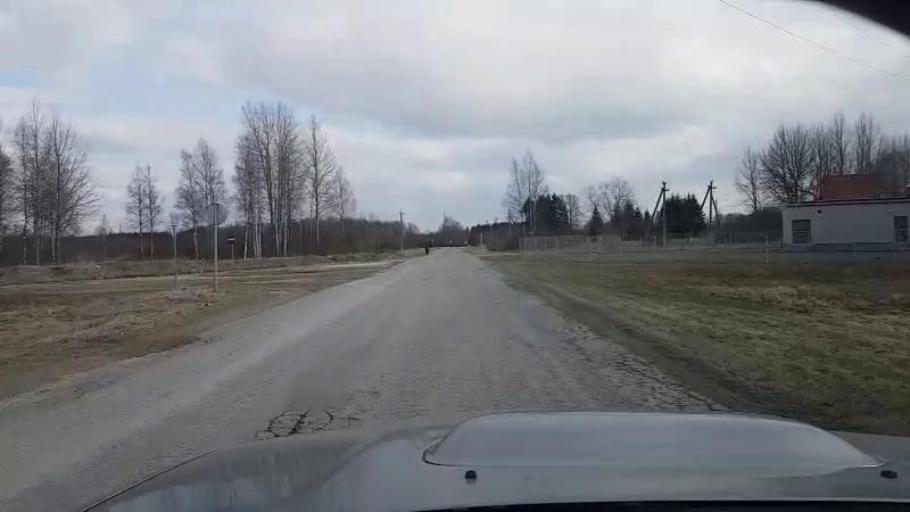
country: EE
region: Jaervamaa
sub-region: Paide linn
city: Paide
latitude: 58.8783
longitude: 25.5503
